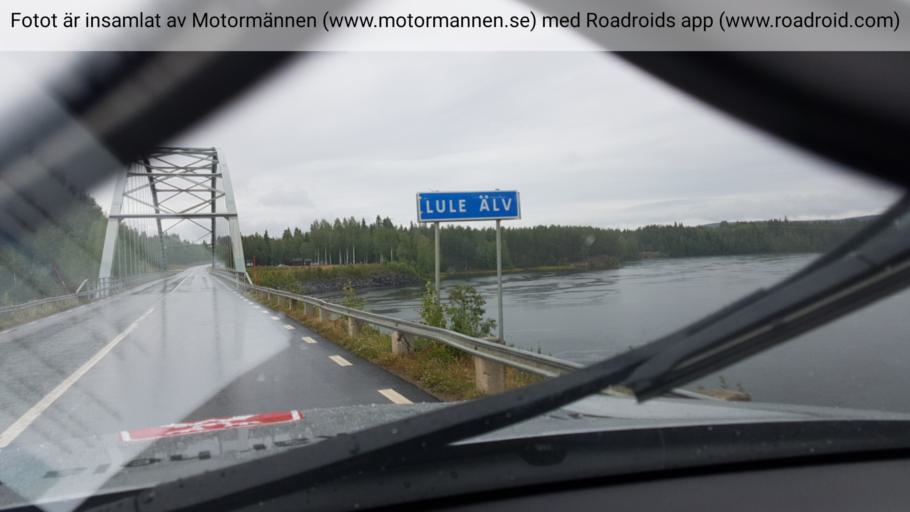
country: SE
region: Norrbotten
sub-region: Alvsbyns Kommun
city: AElvsbyn
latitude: 66.2309
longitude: 20.8719
